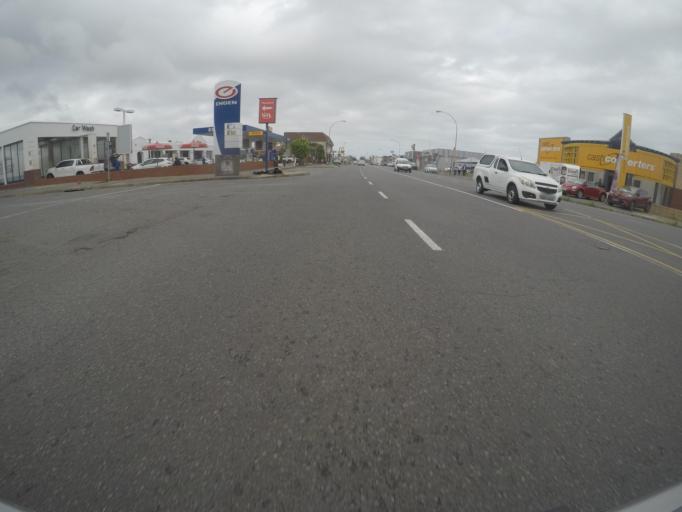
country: ZA
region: Eastern Cape
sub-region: Buffalo City Metropolitan Municipality
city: East London
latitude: -32.9843
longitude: 27.8990
